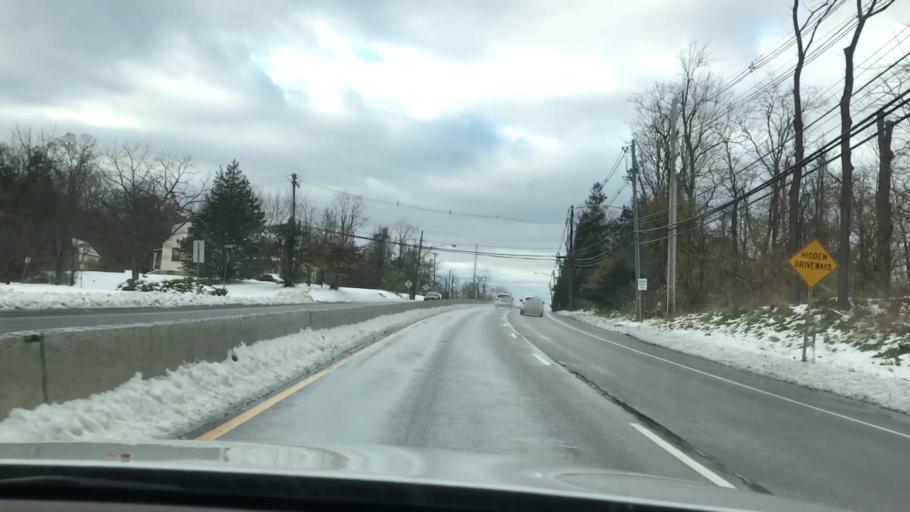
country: US
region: New Jersey
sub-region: Morris County
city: Parsippany
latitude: 40.8268
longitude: -74.4258
